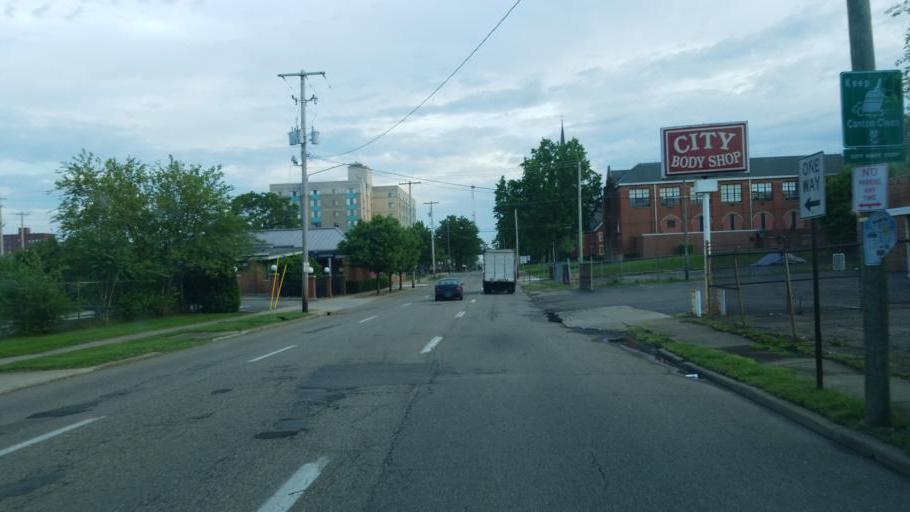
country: US
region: Ohio
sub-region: Stark County
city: Canton
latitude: 40.8053
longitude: -81.3763
